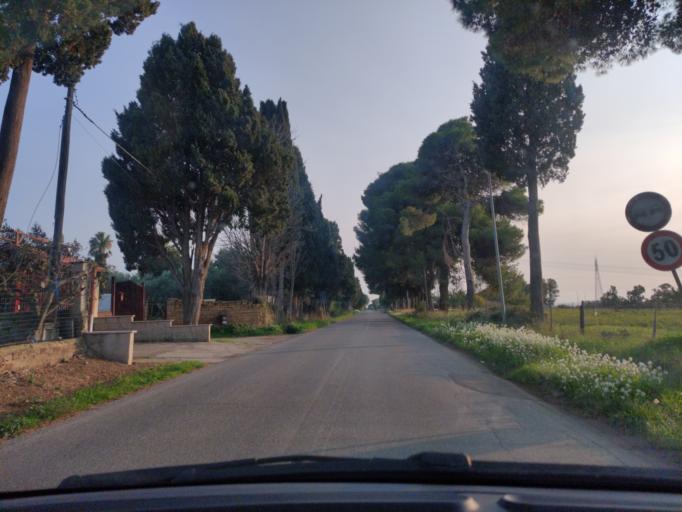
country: IT
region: Latium
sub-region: Citta metropolitana di Roma Capitale
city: Aurelia
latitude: 42.1363
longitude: 11.7884
